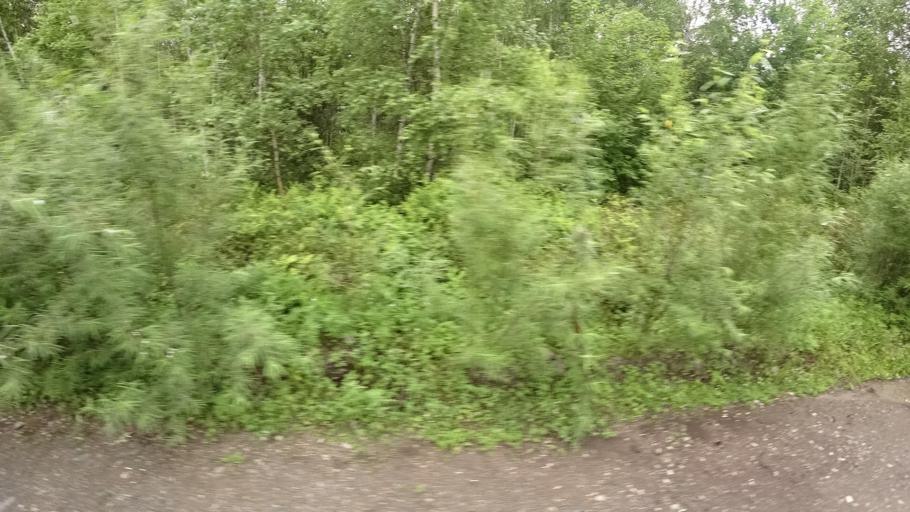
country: RU
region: Khabarovsk Krai
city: Amursk
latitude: 49.9134
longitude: 136.1590
